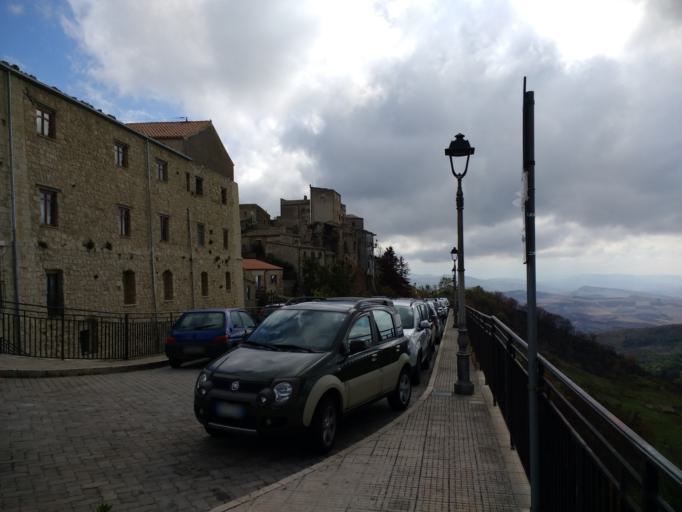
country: IT
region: Sicily
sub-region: Palermo
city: Petralia Soprana
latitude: 37.7961
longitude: 14.1075
